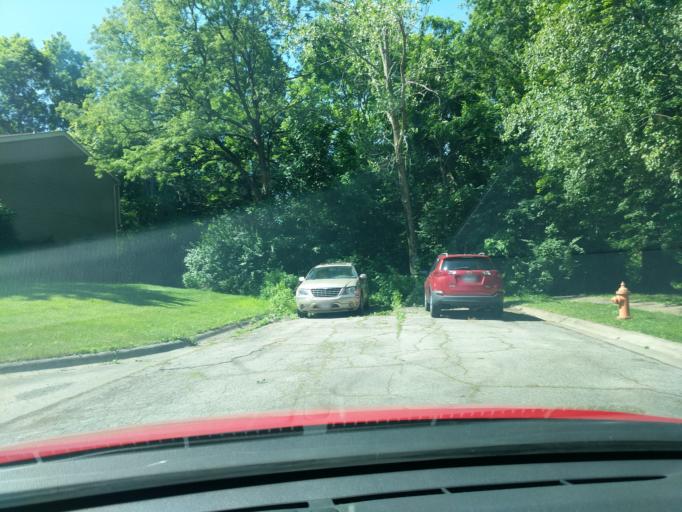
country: US
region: Ohio
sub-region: Franklin County
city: Huber Ridge
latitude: 40.0662
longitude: -82.9169
